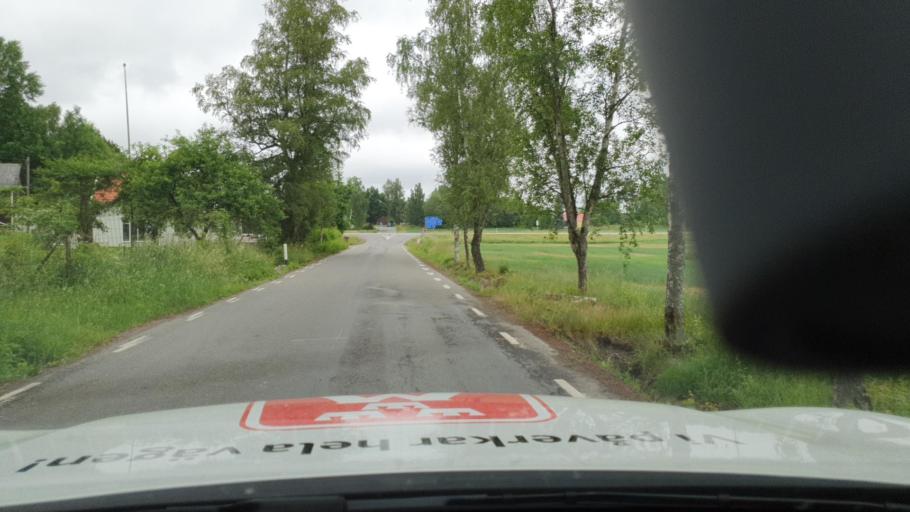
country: SE
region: Vaestra Goetaland
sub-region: Tibro Kommun
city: Tibro
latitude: 58.4134
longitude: 14.0677
